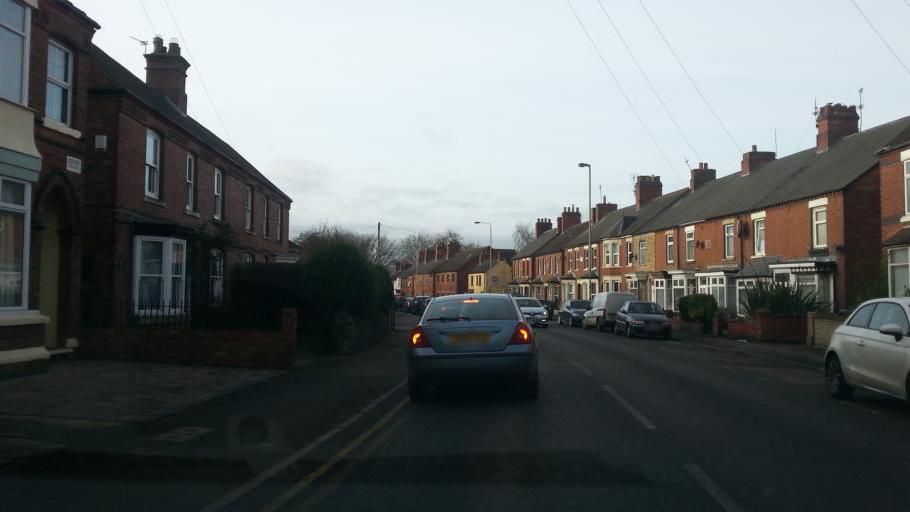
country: GB
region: England
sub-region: Leicestershire
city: Melton Mowbray
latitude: 52.7670
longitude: -0.8771
